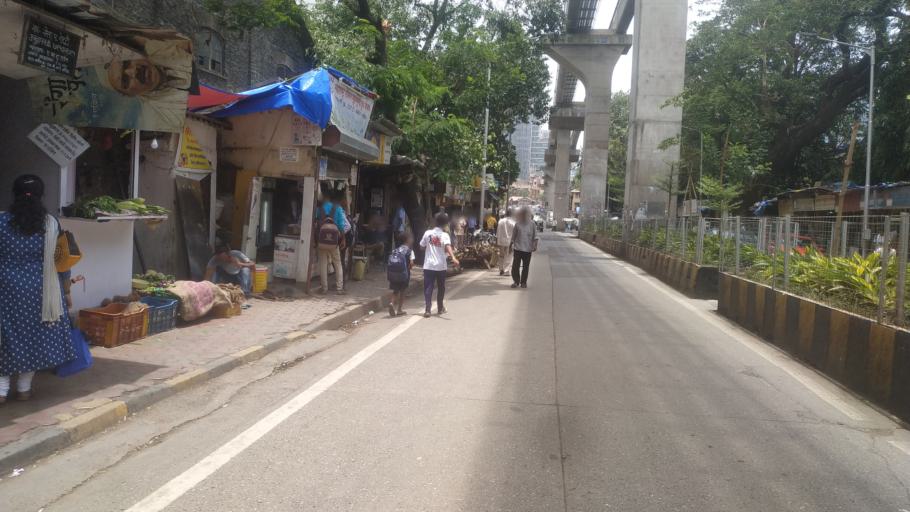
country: IN
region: Maharashtra
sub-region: Mumbai Suburban
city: Mumbai
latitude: 18.9954
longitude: 72.8359
